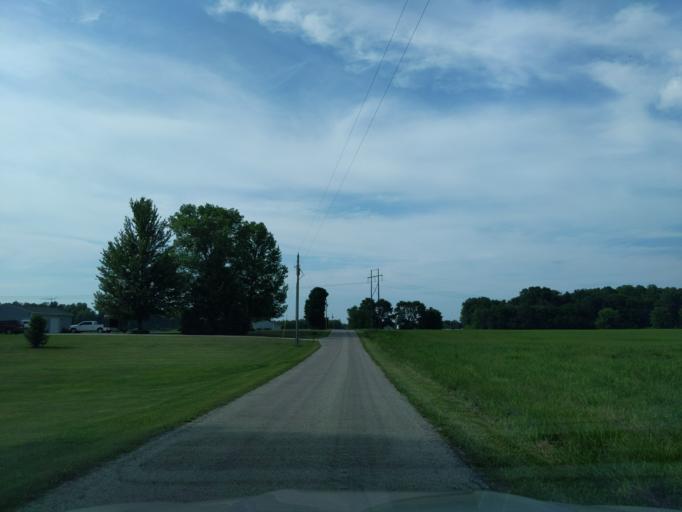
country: US
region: Indiana
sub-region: Ripley County
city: Osgood
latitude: 39.2020
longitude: -85.3892
